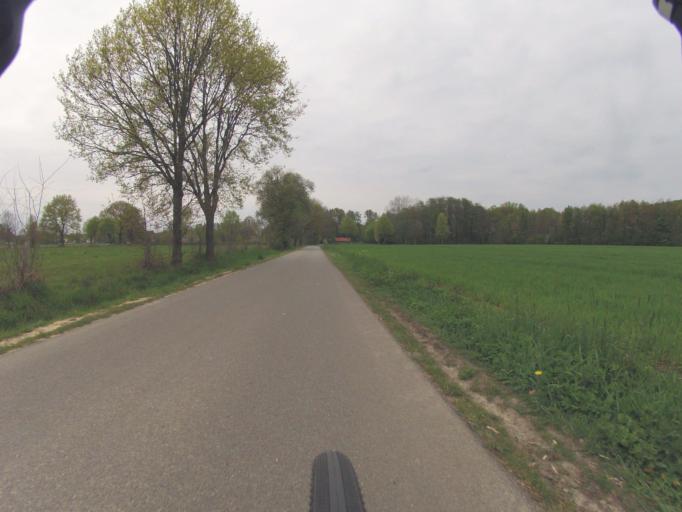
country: DE
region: North Rhine-Westphalia
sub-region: Regierungsbezirk Munster
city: Mettingen
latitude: 52.2905
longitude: 7.8311
